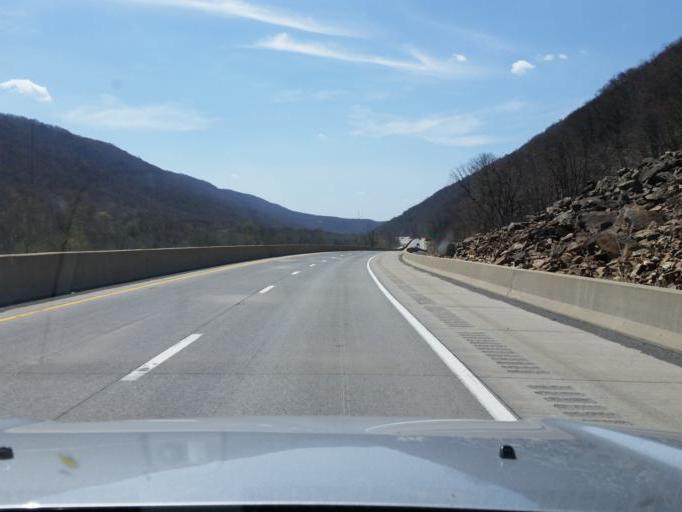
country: US
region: Pennsylvania
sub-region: Mifflin County
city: Lewistown
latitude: 40.5968
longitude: -77.5000
